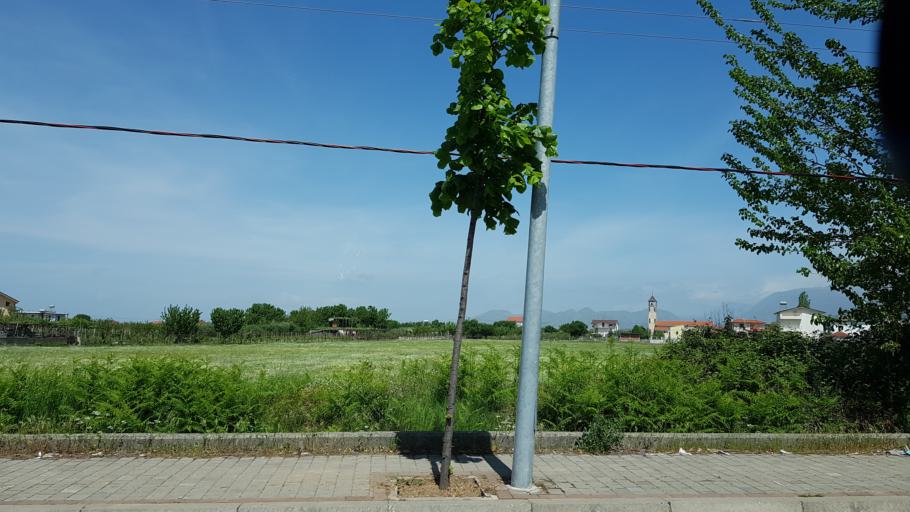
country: AL
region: Shkoder
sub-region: Rrethi i Shkodres
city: Shkoder
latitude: 42.1013
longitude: 19.5494
